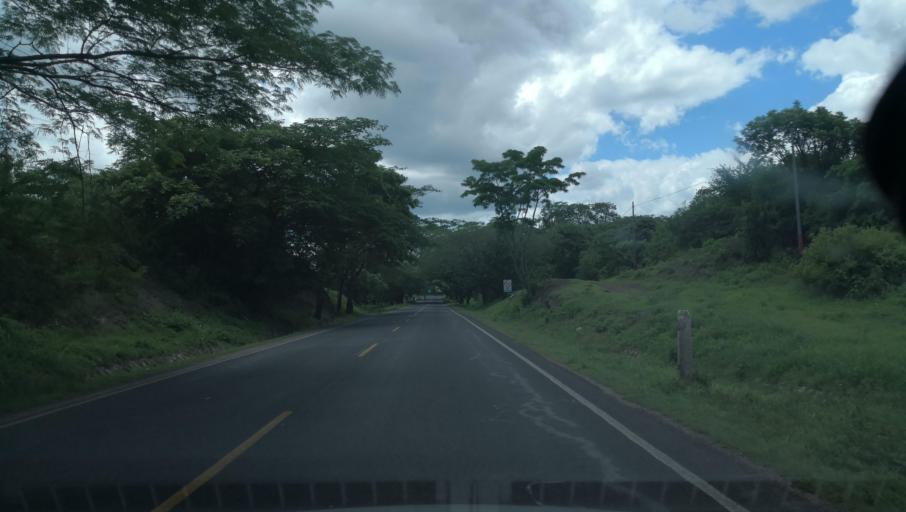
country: NI
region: Madriz
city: Palacaguina
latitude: 13.4278
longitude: -86.4059
